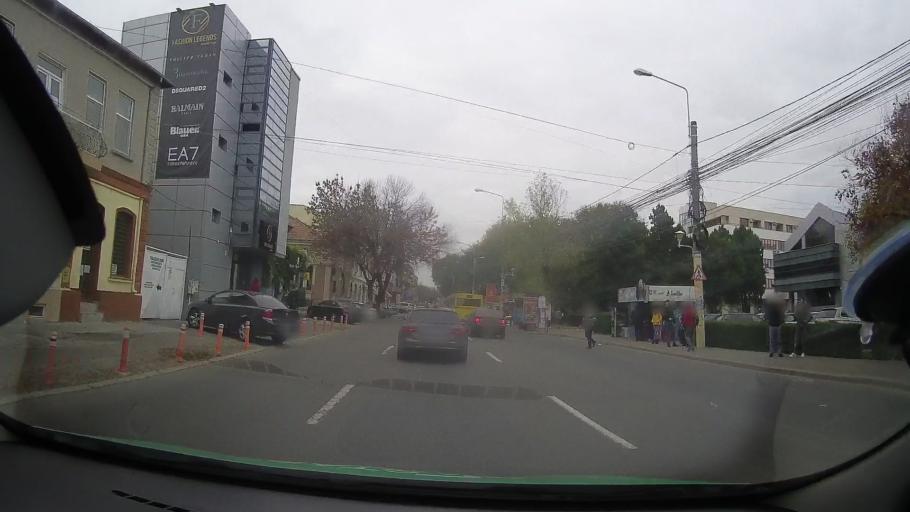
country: RO
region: Constanta
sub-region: Municipiul Constanta
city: Constanta
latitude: 44.1827
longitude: 28.6498
